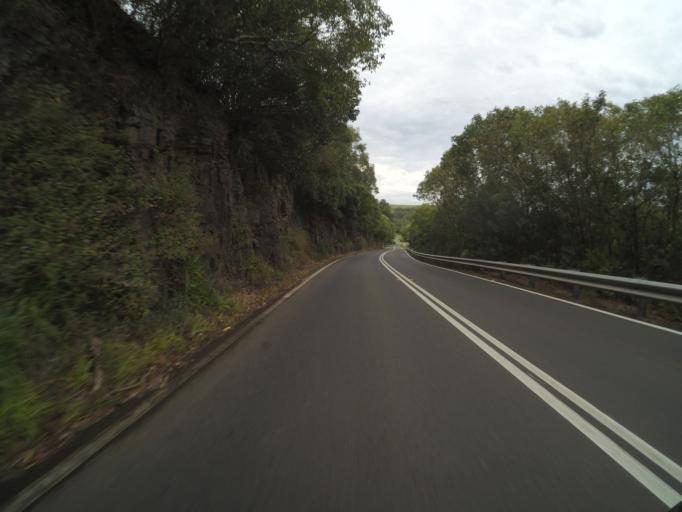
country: AU
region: New South Wales
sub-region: Kiama
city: Kiama
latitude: -34.6649
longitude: 150.8366
